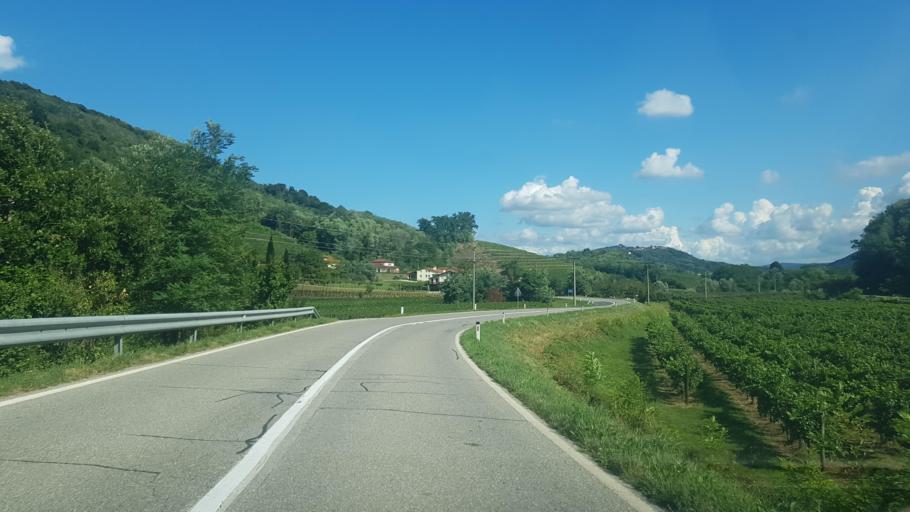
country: SI
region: Nova Gorica
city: Prvacina
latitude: 45.8760
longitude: 13.7592
